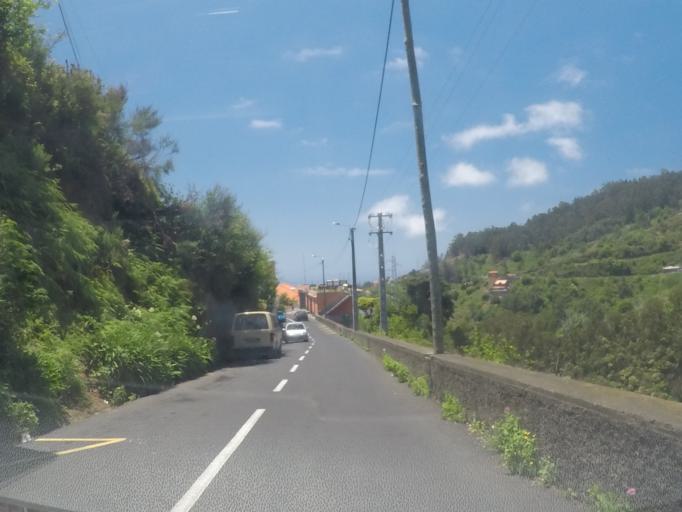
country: PT
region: Madeira
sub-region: Camara de Lobos
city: Curral das Freiras
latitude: 32.6817
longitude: -16.9907
